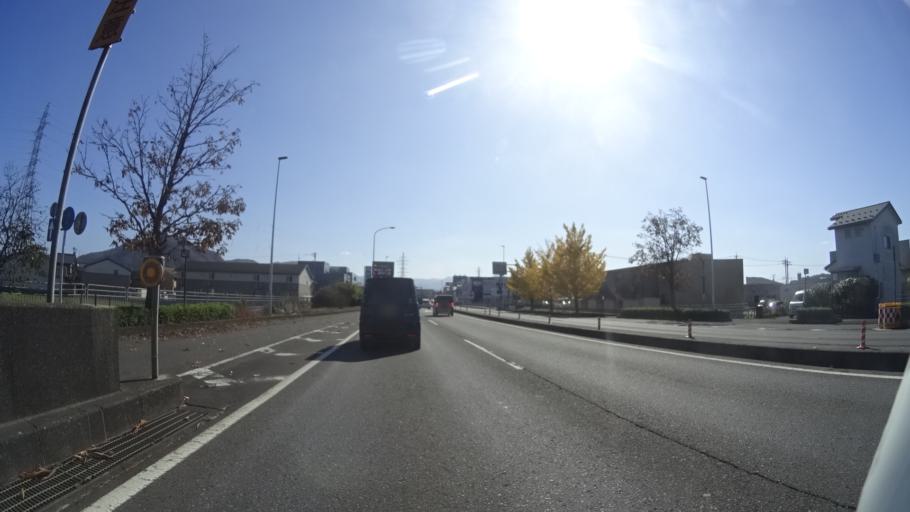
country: JP
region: Fukui
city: Sabae
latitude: 35.9513
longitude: 136.1920
